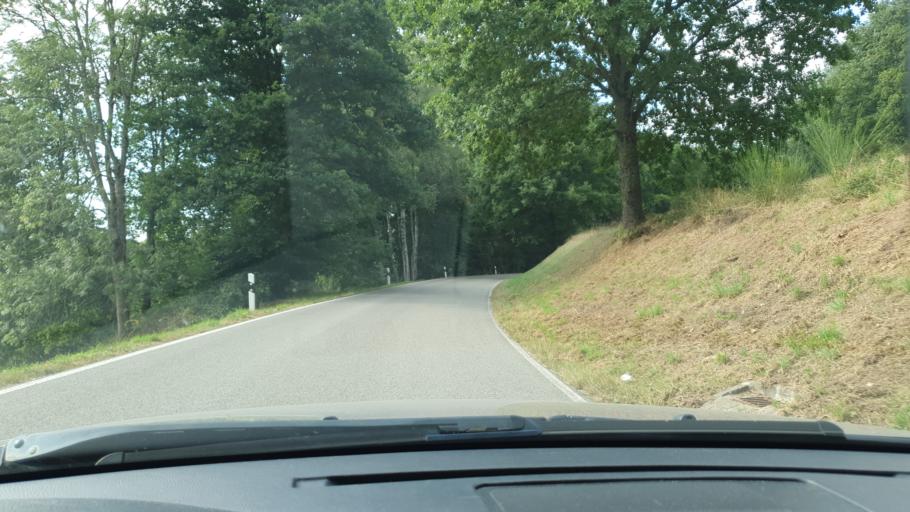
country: DE
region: Rheinland-Pfalz
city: Gerhardsbrunn
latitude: 49.3376
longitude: 7.5232
